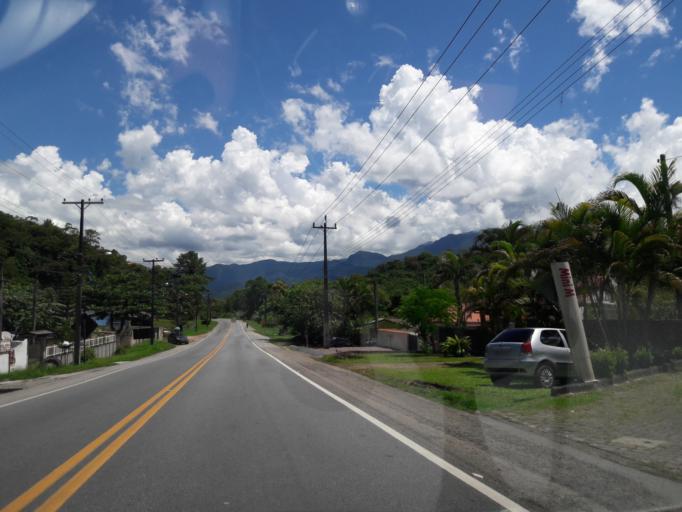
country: BR
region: Parana
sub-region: Antonina
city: Antonina
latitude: -25.4624
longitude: -48.8219
